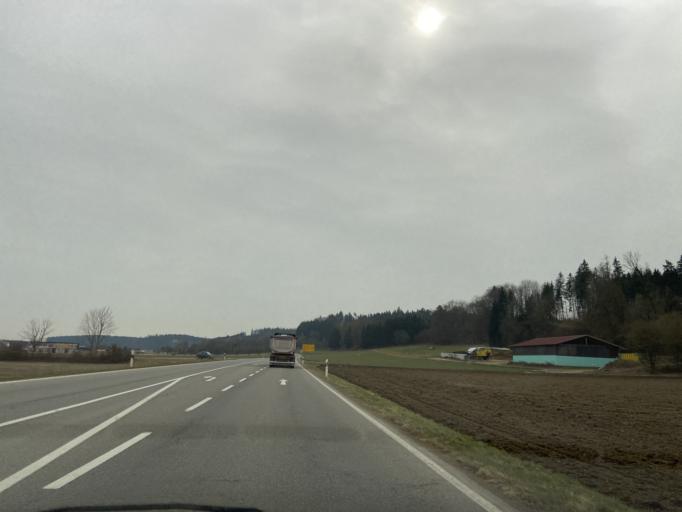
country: DE
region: Baden-Wuerttemberg
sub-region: Tuebingen Region
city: Ostrach
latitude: 47.9781
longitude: 9.3444
